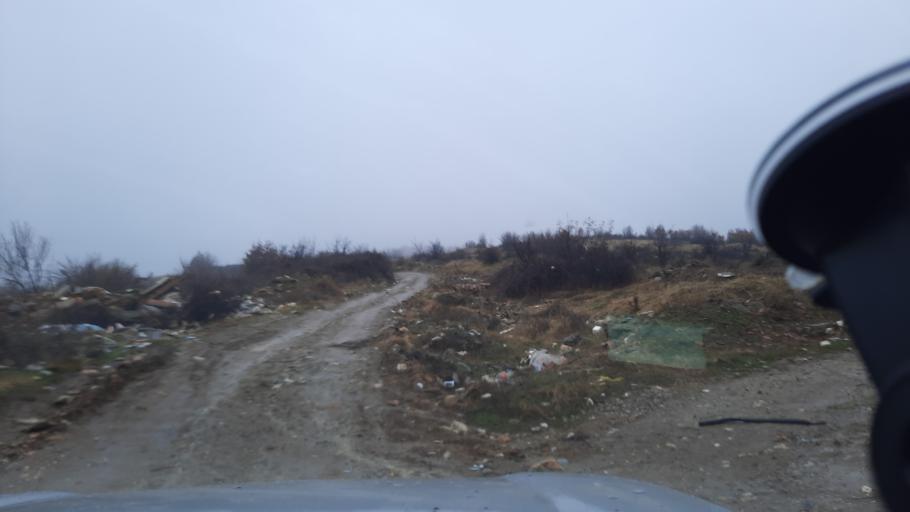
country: MK
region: Opstina Lipkovo
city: Matejche
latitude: 42.1247
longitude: 21.5845
